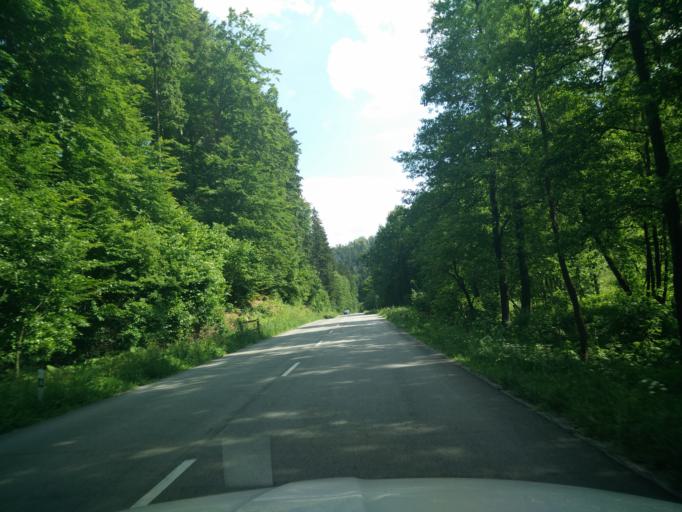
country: SK
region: Zilinsky
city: Rajec
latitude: 48.9389
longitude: 18.6306
